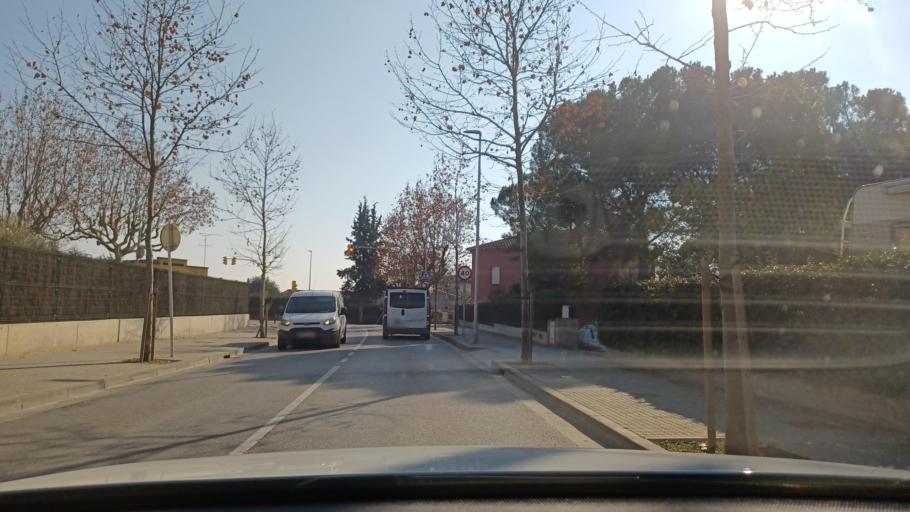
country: ES
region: Catalonia
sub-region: Provincia de Barcelona
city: L'Ametlla del Valles
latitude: 41.6658
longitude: 2.2620
